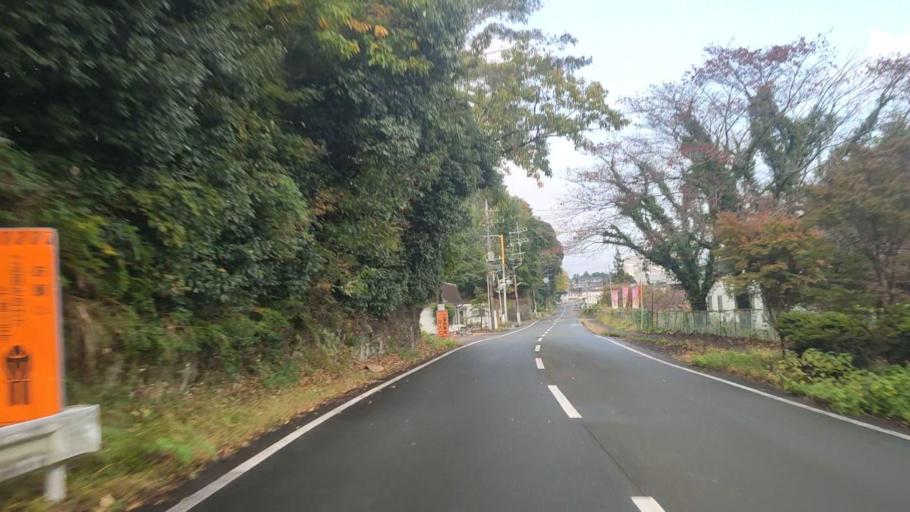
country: JP
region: Shizuoka
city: Fujinomiya
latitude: 35.2937
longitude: 138.4517
